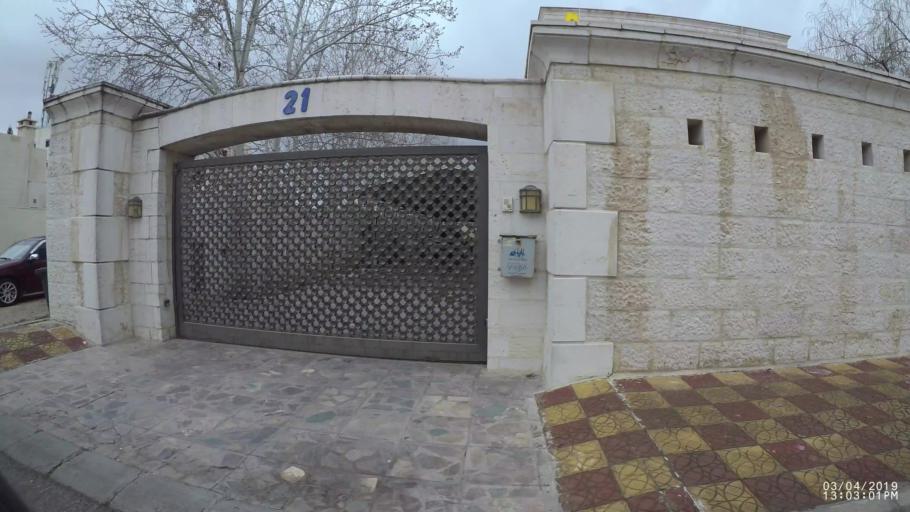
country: JO
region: Amman
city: Wadi as Sir
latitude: 31.9669
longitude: 35.8277
